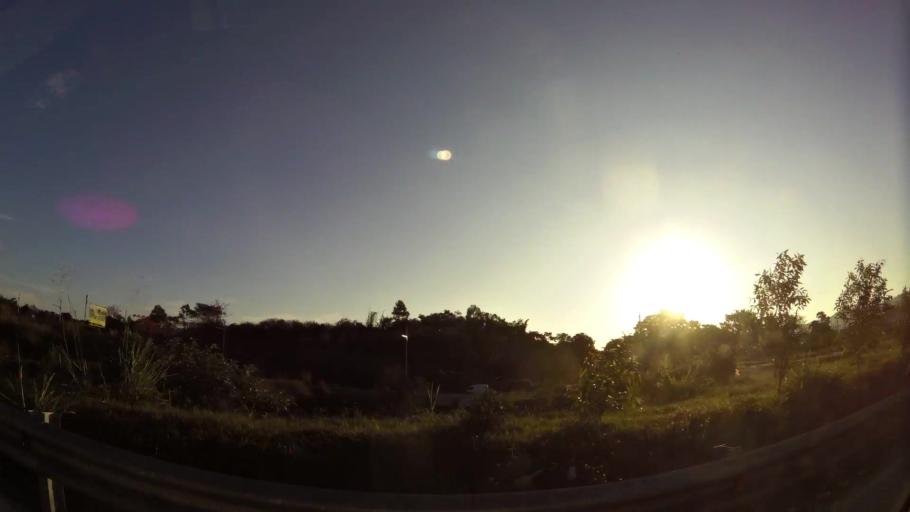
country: SV
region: La Libertad
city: Santa Tecla
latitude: 13.6821
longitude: -89.2638
